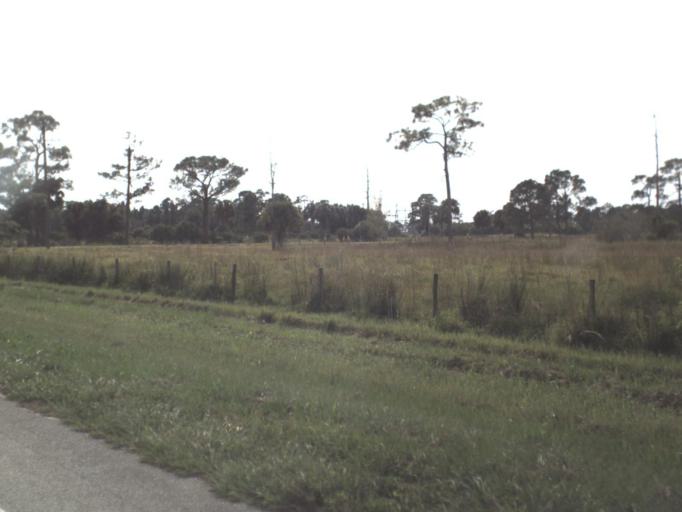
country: US
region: Florida
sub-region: Okeechobee County
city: Cypress Quarters
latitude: 27.2909
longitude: -80.8280
